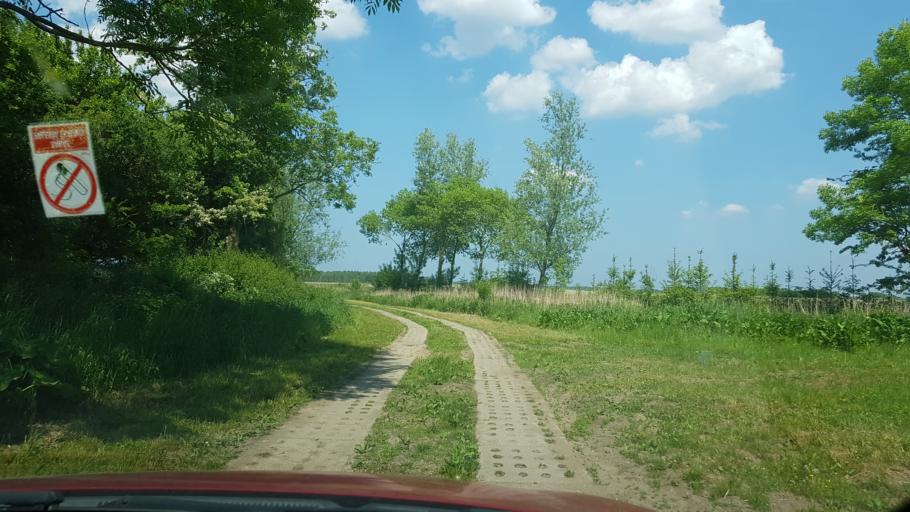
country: PL
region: West Pomeranian Voivodeship
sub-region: Powiat gryficki
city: Trzebiatow
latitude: 54.0934
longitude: 15.2122
